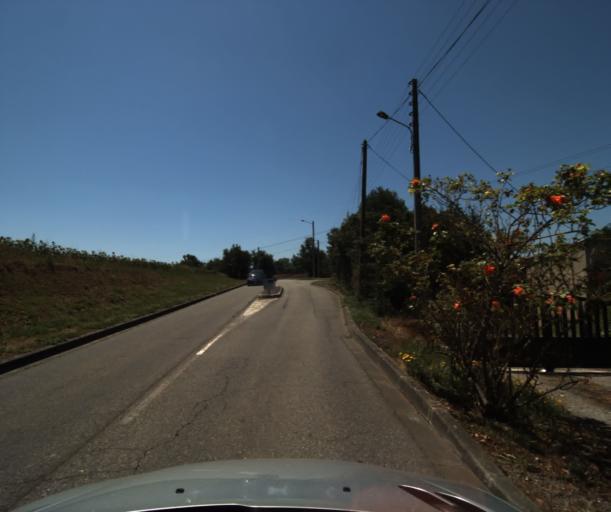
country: FR
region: Midi-Pyrenees
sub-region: Departement de la Haute-Garonne
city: Pinsaguel
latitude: 43.5051
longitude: 1.3795
